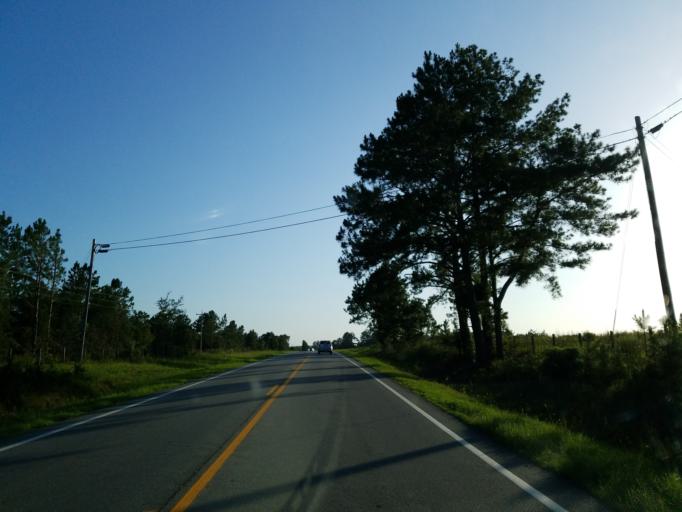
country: US
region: Georgia
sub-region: Irwin County
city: Ocilla
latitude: 31.6397
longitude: -83.4048
